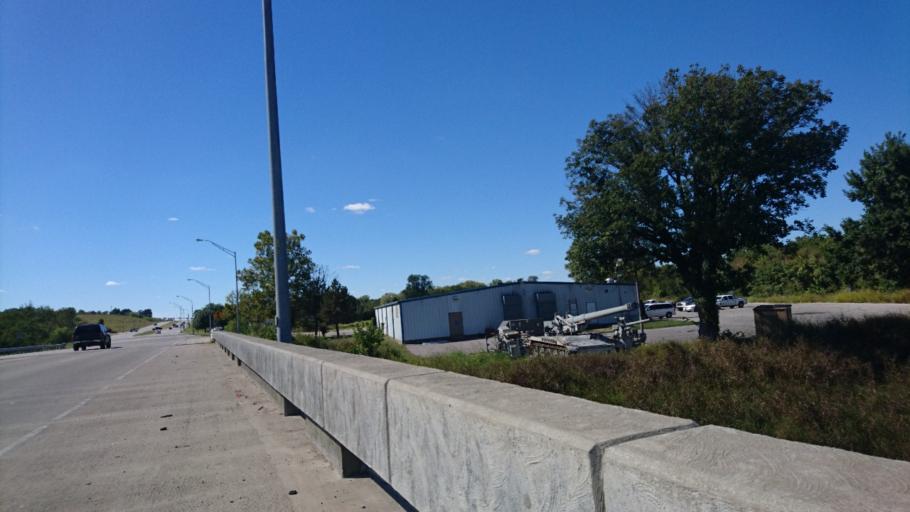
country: US
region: Oklahoma
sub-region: Creek County
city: Sapulpa
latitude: 35.9933
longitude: -96.1367
